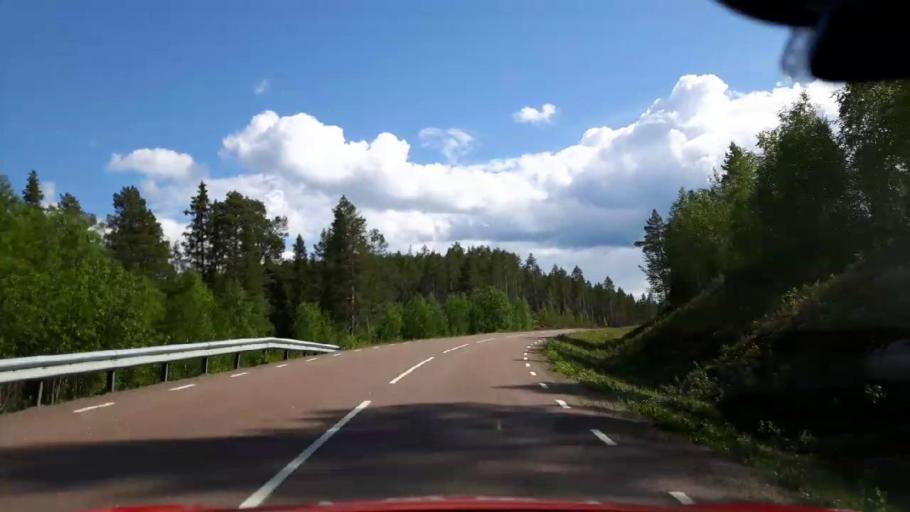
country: SE
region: Jaemtland
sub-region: Krokoms Kommun
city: Valla
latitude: 64.0052
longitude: 14.2399
